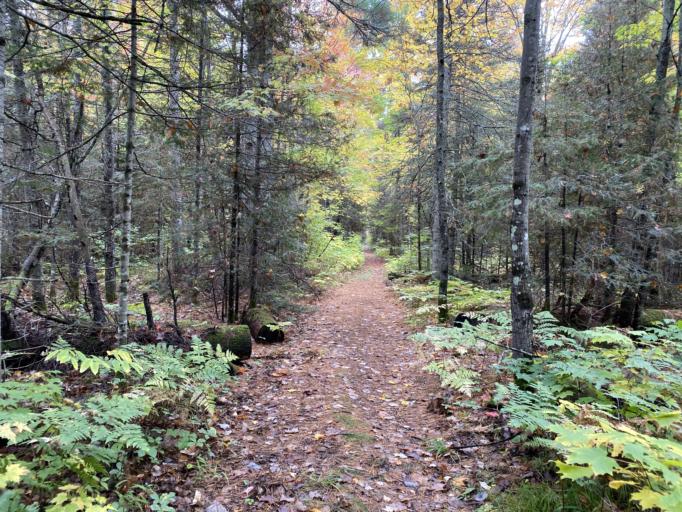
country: US
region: Michigan
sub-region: Marquette County
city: West Ishpeming
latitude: 46.5351
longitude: -87.9996
